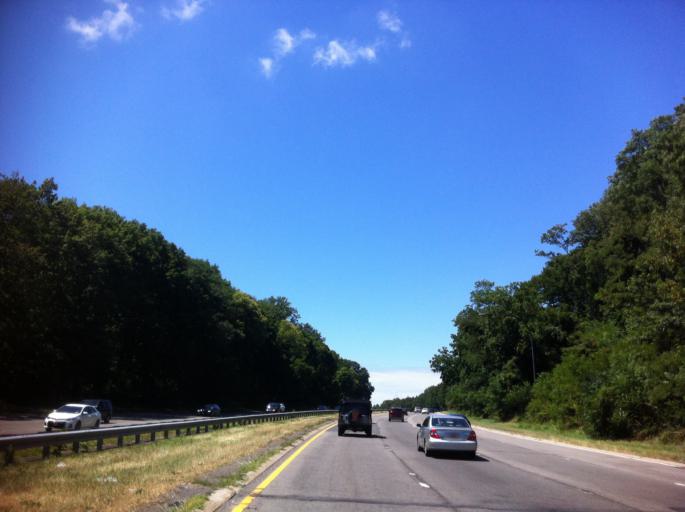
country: US
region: New York
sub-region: Nassau County
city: Manhasset Hills
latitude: 40.7634
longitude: -73.6927
